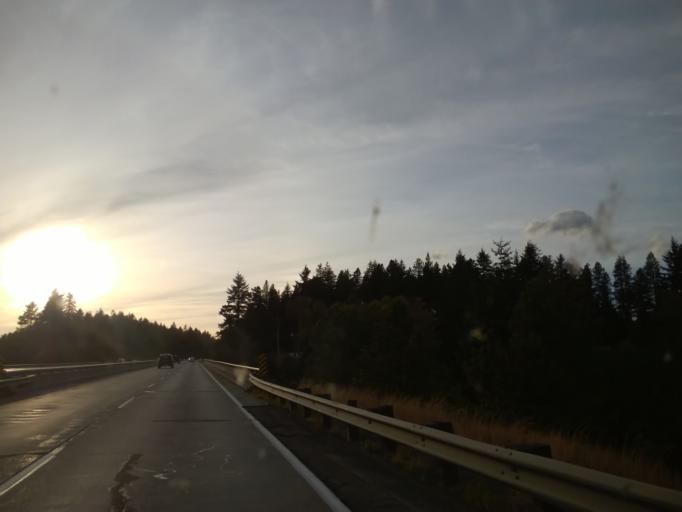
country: US
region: Washington
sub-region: Kittitas County
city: Cle Elum
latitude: 47.1929
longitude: -120.9486
